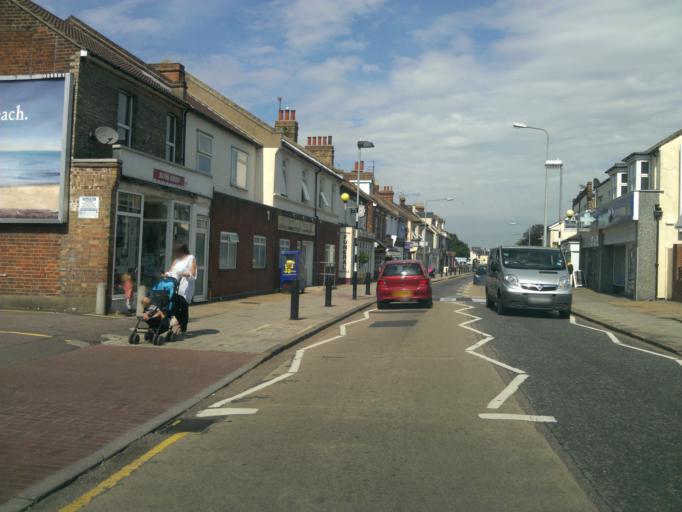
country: GB
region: England
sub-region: Essex
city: Clacton-on-Sea
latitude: 51.7948
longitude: 1.1484
